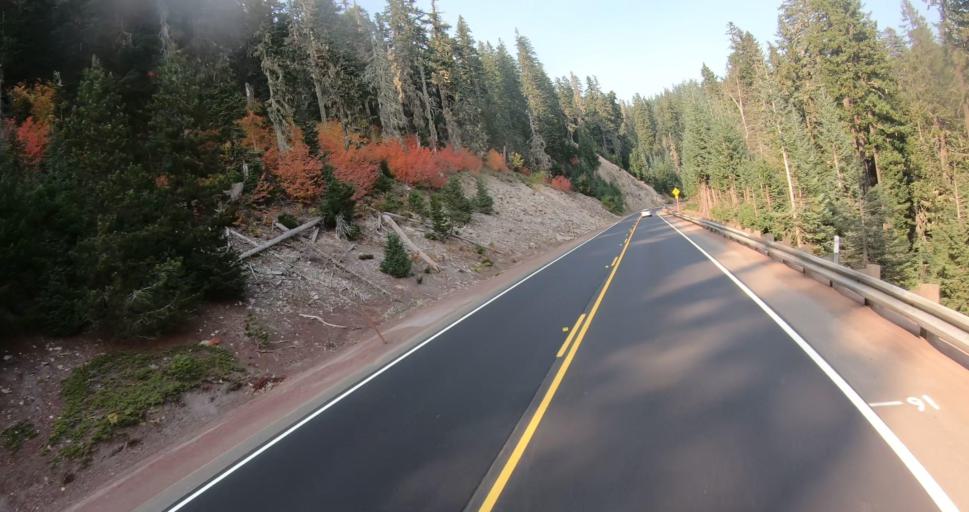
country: US
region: Oregon
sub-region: Clackamas County
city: Mount Hood Village
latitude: 45.3108
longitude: -121.6618
